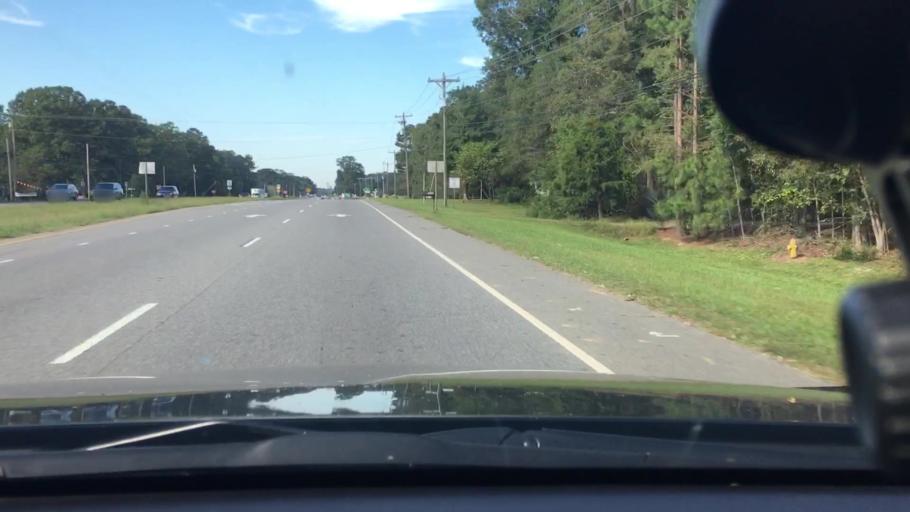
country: US
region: North Carolina
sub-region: Cabarrus County
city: Midland
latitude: 35.2551
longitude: -80.4818
